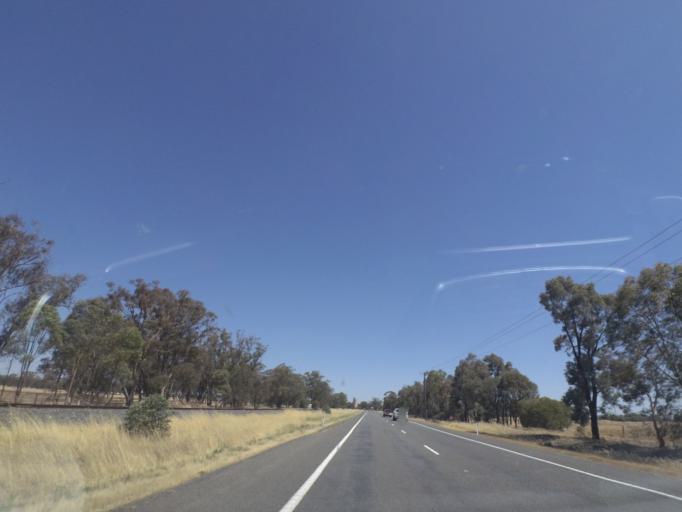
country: AU
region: Victoria
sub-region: Greater Shepparton
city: Shepparton
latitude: -36.2293
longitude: 145.4318
